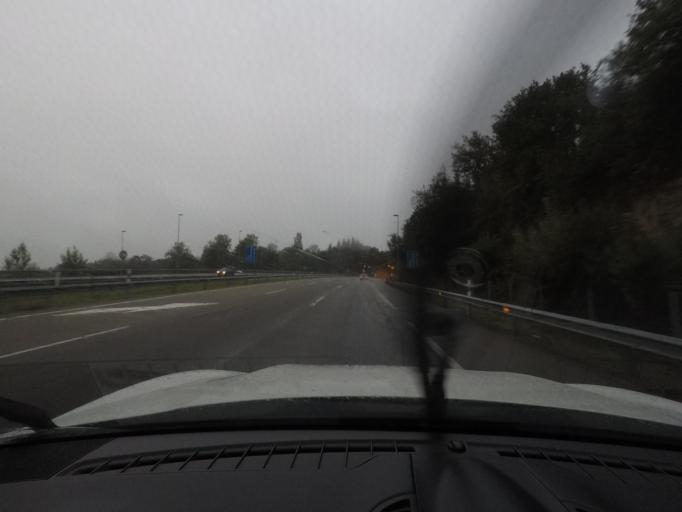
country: ES
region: Asturias
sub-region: Province of Asturias
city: Oviedo
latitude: 43.3441
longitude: -5.8886
